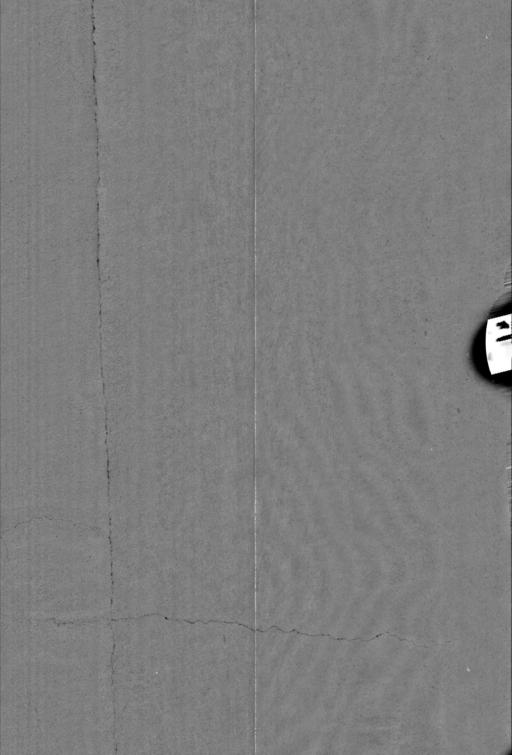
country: US
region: Maryland
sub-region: Prince George's County
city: Glassmanor
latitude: 38.8321
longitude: -76.9926
